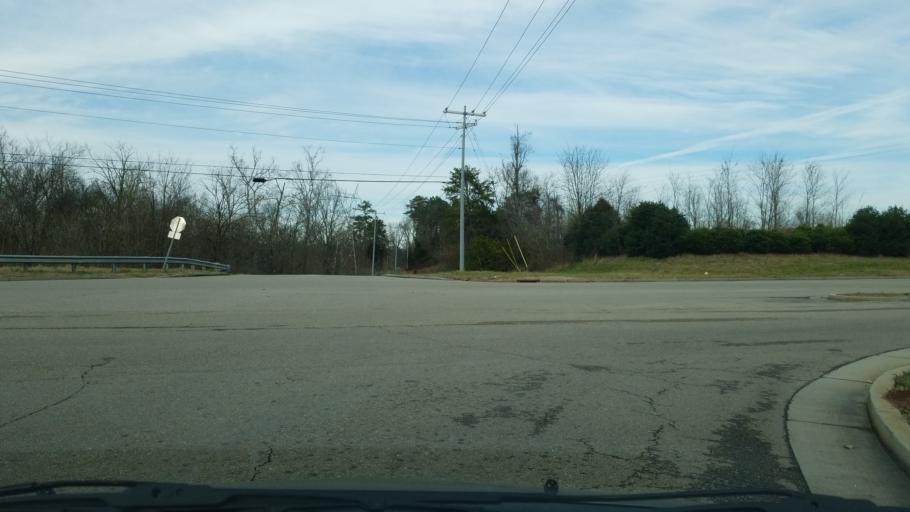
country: US
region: Tennessee
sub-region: Loudon County
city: Lenoir City
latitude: 35.8209
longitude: -84.2739
